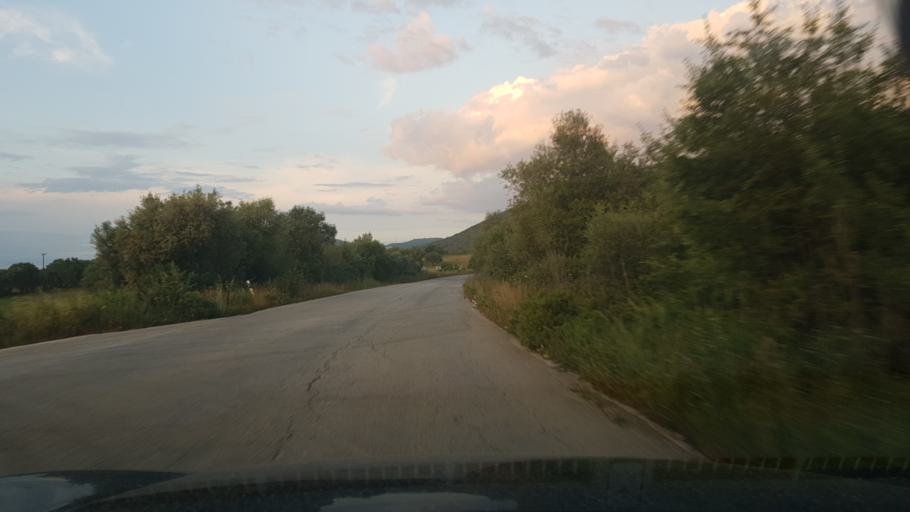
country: GR
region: West Greece
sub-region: Nomos Aitolias kai Akarnanias
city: Vonitsa
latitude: 38.8972
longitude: 20.8651
